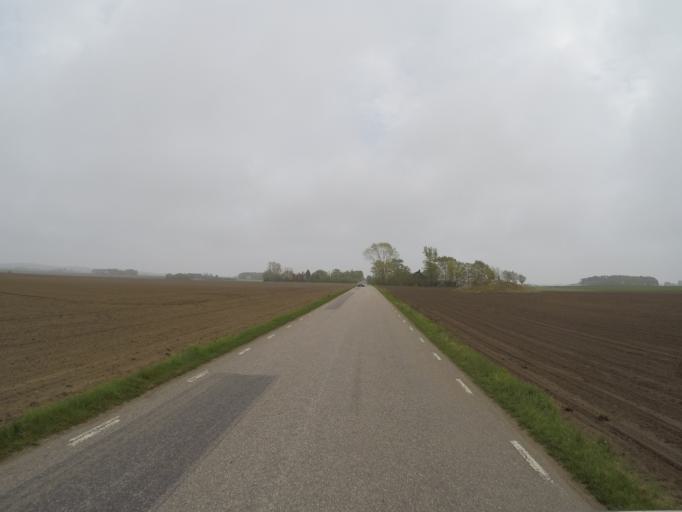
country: SE
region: Halland
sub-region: Laholms Kommun
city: Laholm
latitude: 56.5271
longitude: 12.9942
